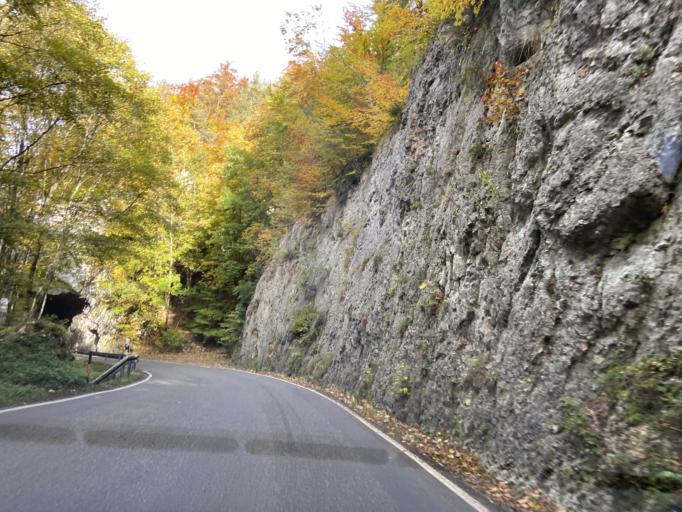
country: DE
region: Baden-Wuerttemberg
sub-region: Tuebingen Region
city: Leibertingen
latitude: 48.0665
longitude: 9.0357
